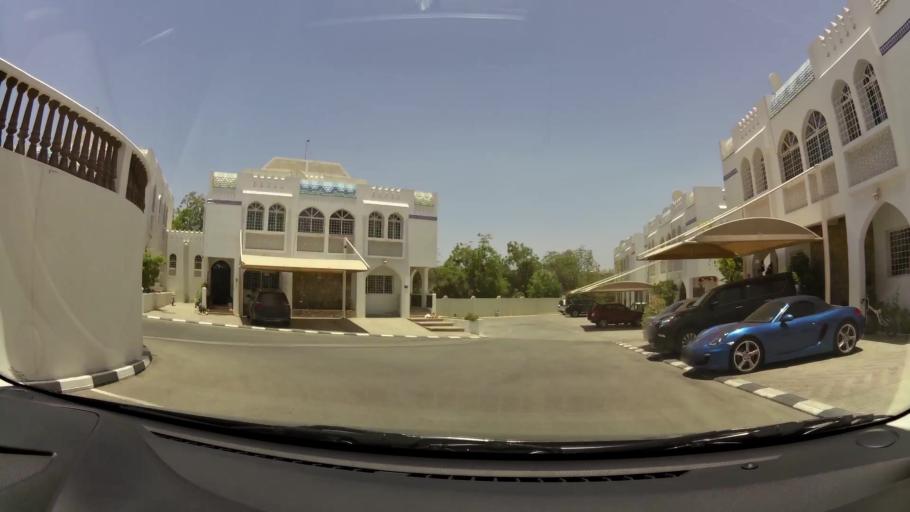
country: OM
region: Muhafazat Masqat
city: Bawshar
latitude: 23.6070
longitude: 58.4883
